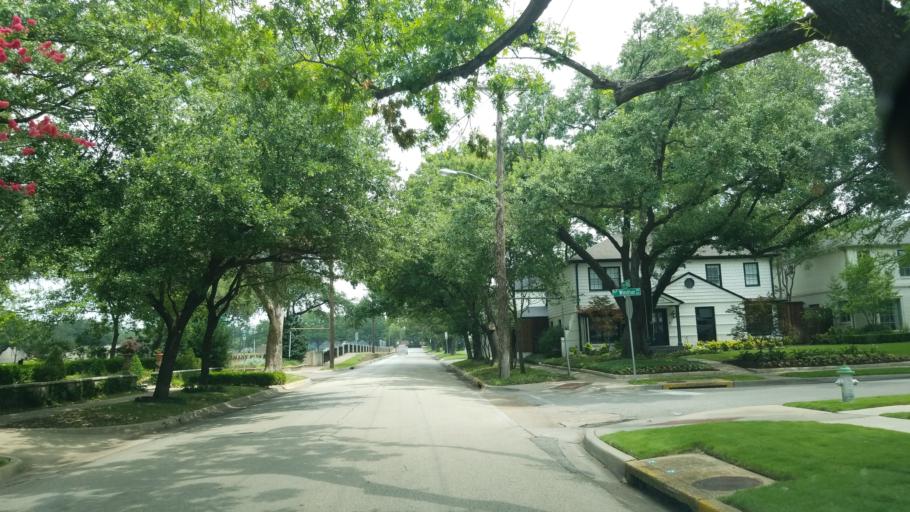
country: US
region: Texas
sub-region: Dallas County
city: University Park
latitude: 32.8423
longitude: -96.8130
